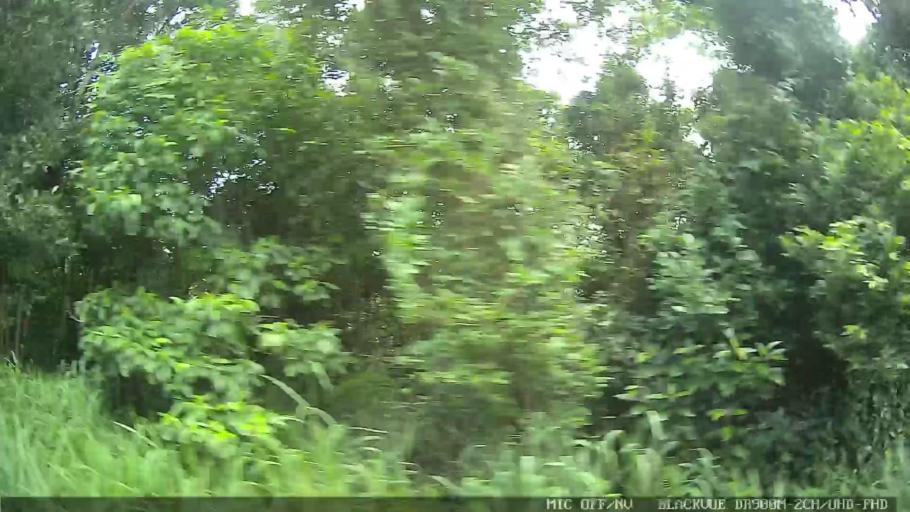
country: BR
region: Sao Paulo
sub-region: Iguape
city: Iguape
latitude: -24.6863
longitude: -47.4936
